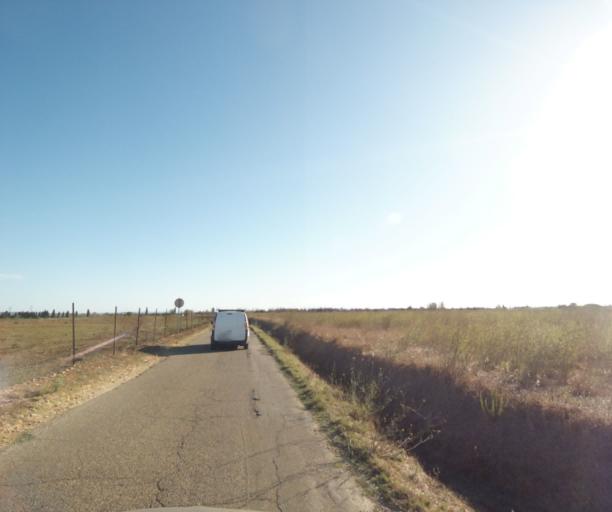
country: FR
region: Languedoc-Roussillon
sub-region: Departement du Gard
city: Bouillargues
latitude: 43.8003
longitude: 4.4476
